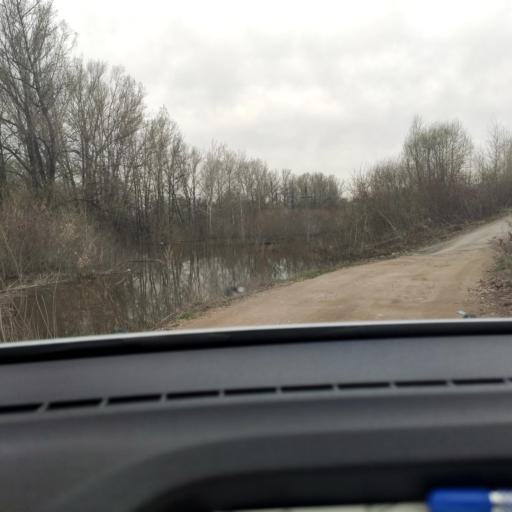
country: RU
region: Bashkortostan
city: Avdon
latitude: 54.6143
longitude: 55.6067
